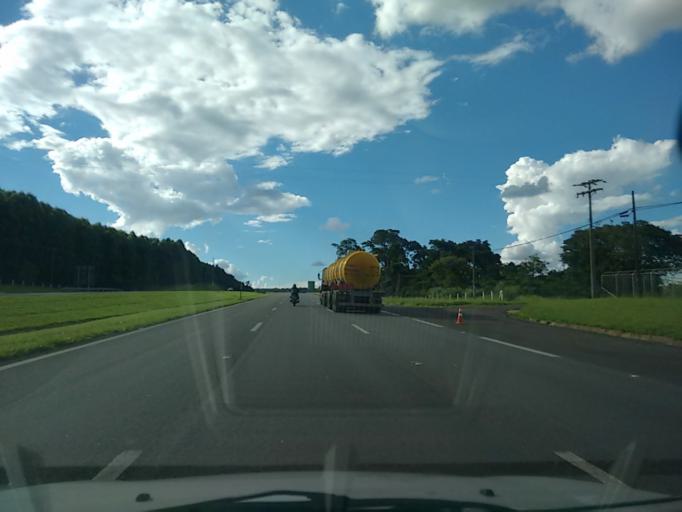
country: BR
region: Sao Paulo
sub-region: Sao Carlos
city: Sao Carlos
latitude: -22.0533
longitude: -47.8564
